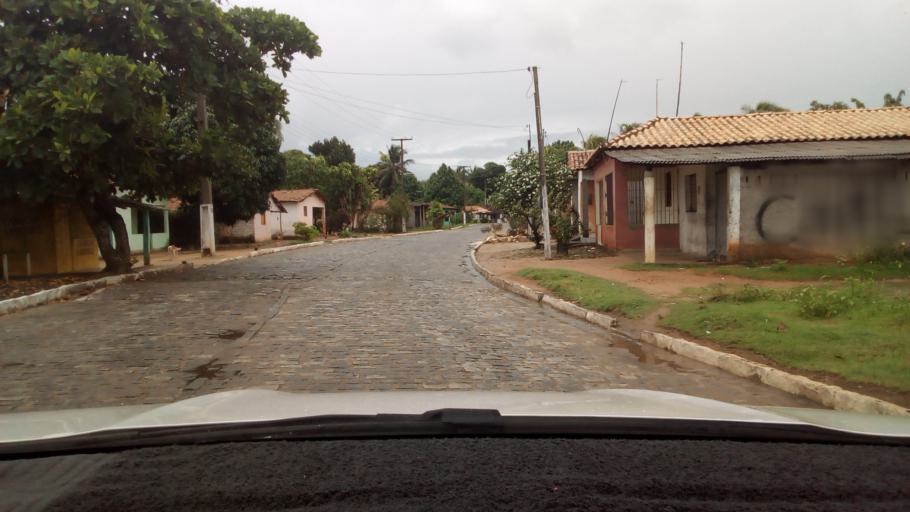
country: BR
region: Paraiba
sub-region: Pitimbu
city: Pitimbu
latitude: -7.4532
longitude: -34.8367
